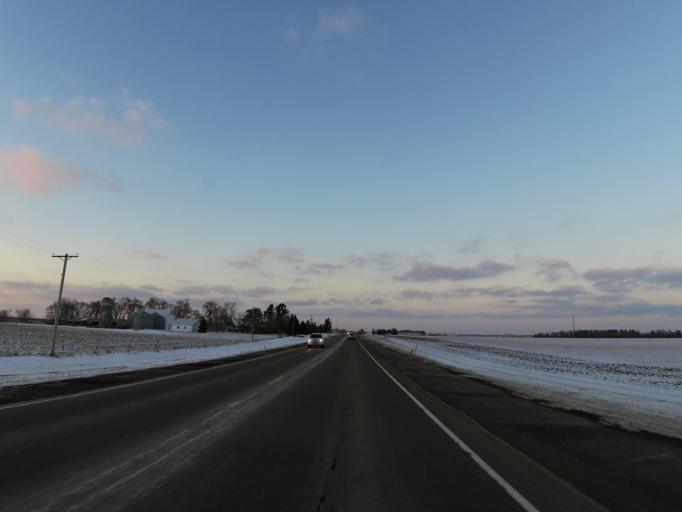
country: US
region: Minnesota
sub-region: Dakota County
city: Rosemount
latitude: 44.6965
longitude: -93.1365
